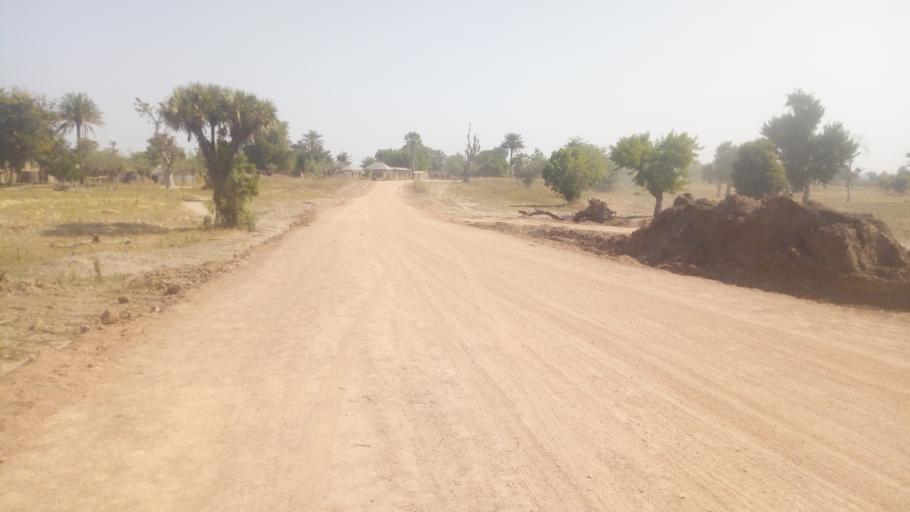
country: NG
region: Adamawa
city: Mayo Belwa
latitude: 9.1566
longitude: 12.0082
